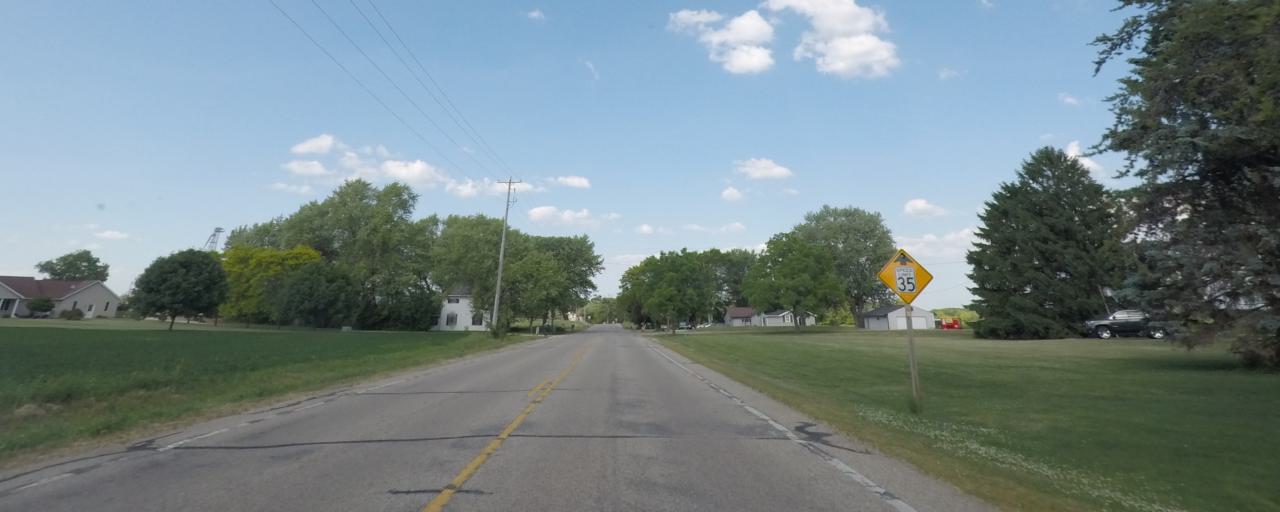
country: US
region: Wisconsin
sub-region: Walworth County
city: Potter Lake
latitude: 42.8185
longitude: -88.3277
